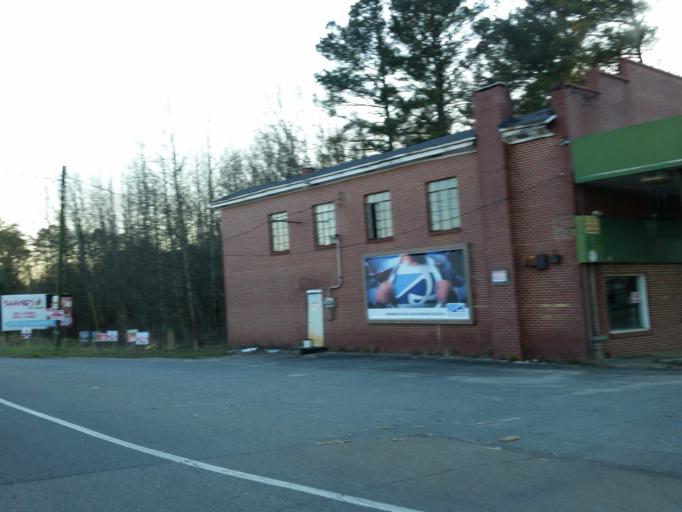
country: US
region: Georgia
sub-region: Cherokee County
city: Holly Springs
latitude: 34.1766
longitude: -84.4204
